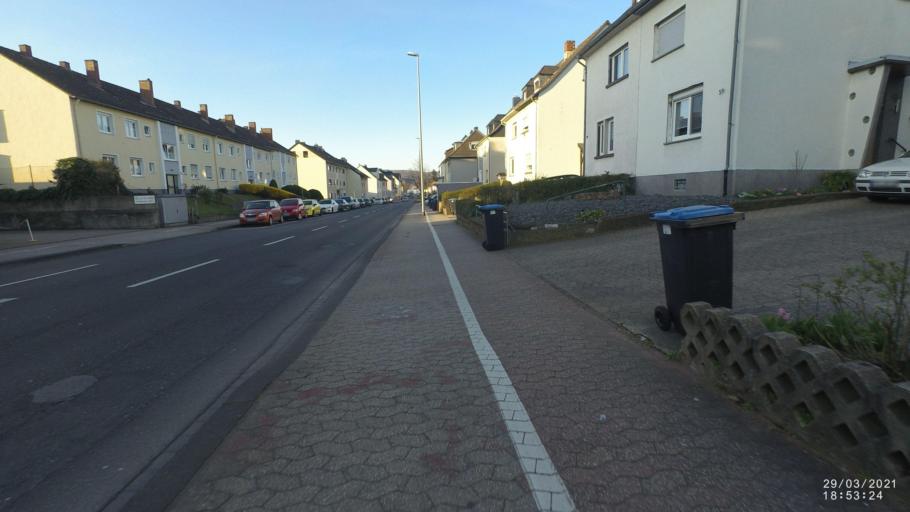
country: DE
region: Rheinland-Pfalz
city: Andernach
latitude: 50.4270
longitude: 7.4074
